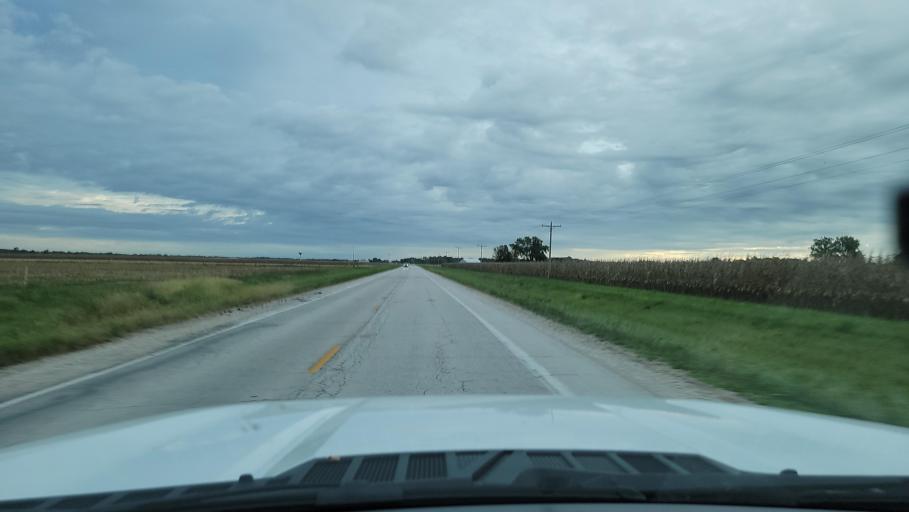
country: US
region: Illinois
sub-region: Schuyler County
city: Rushville
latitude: 40.0980
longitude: -90.6001
